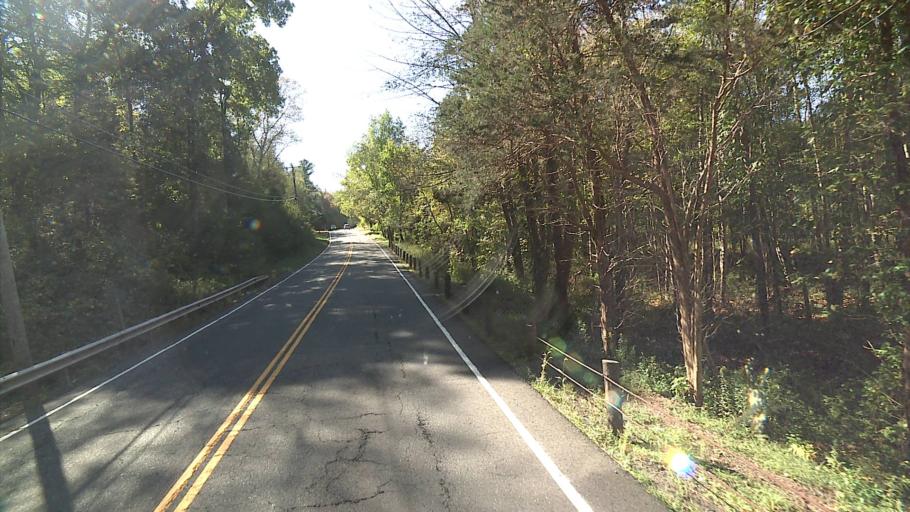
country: US
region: Connecticut
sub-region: Tolland County
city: Somers
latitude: 41.9442
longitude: -72.4502
